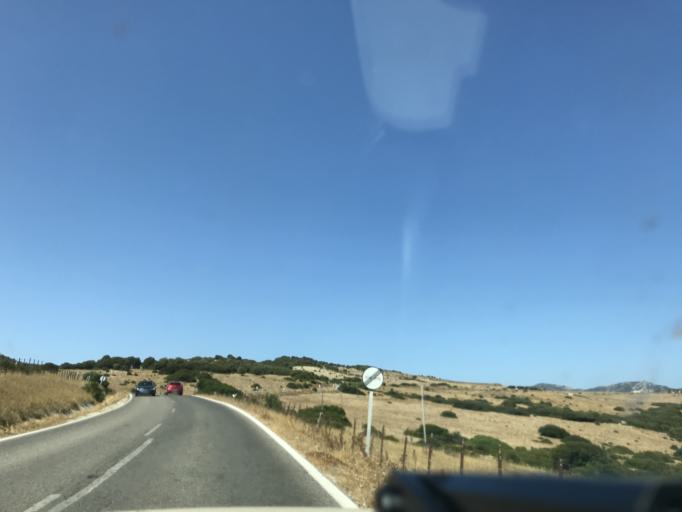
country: ES
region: Andalusia
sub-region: Provincia de Cadiz
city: Zahara de los Atunes
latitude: 36.0992
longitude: -5.7477
